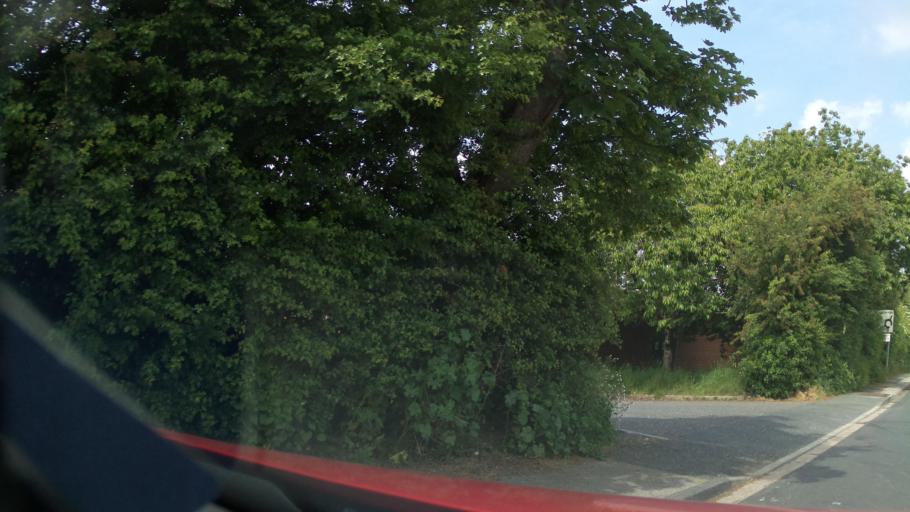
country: GB
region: England
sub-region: North Yorkshire
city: Boroughbridge
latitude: 54.0856
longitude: -1.3961
